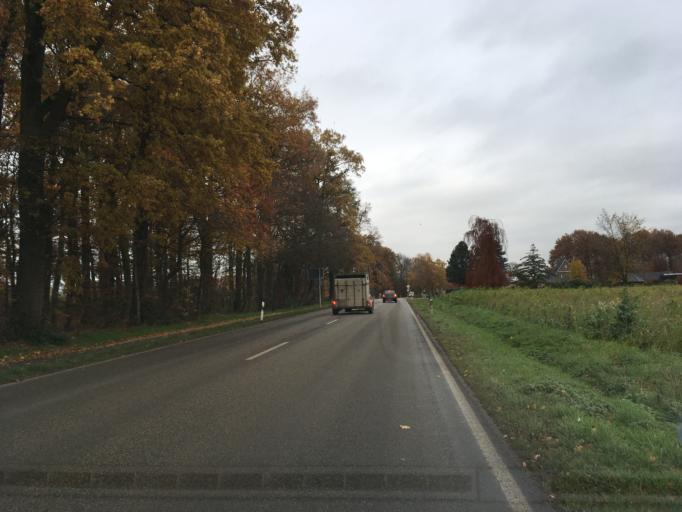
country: DE
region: North Rhine-Westphalia
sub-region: Regierungsbezirk Munster
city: Gescher
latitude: 51.9663
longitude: 7.0126
